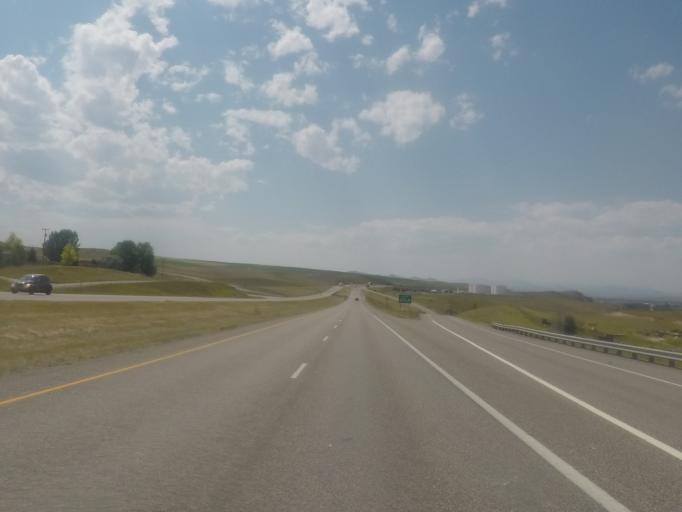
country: US
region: Montana
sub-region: Gallatin County
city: Manhattan
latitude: 45.8820
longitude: -111.4323
